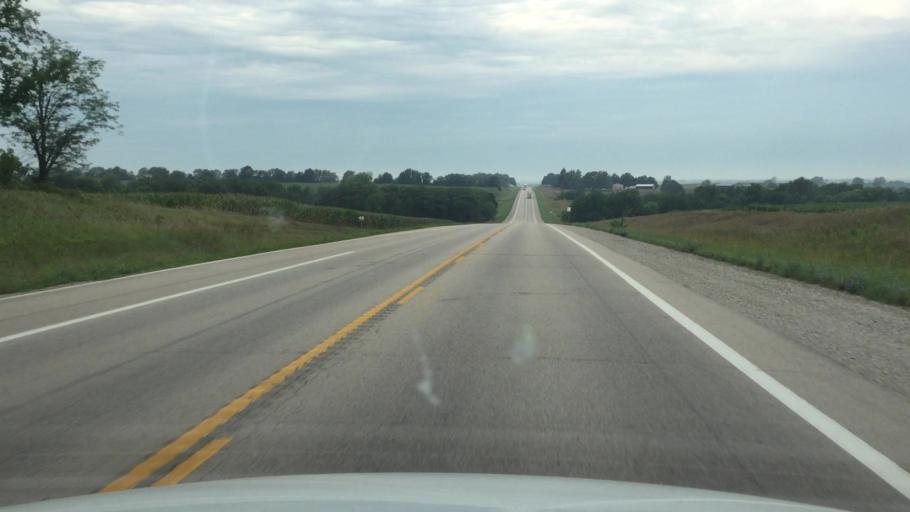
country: US
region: Kansas
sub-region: Brown County
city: Hiawatha
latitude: 39.8486
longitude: -95.6023
